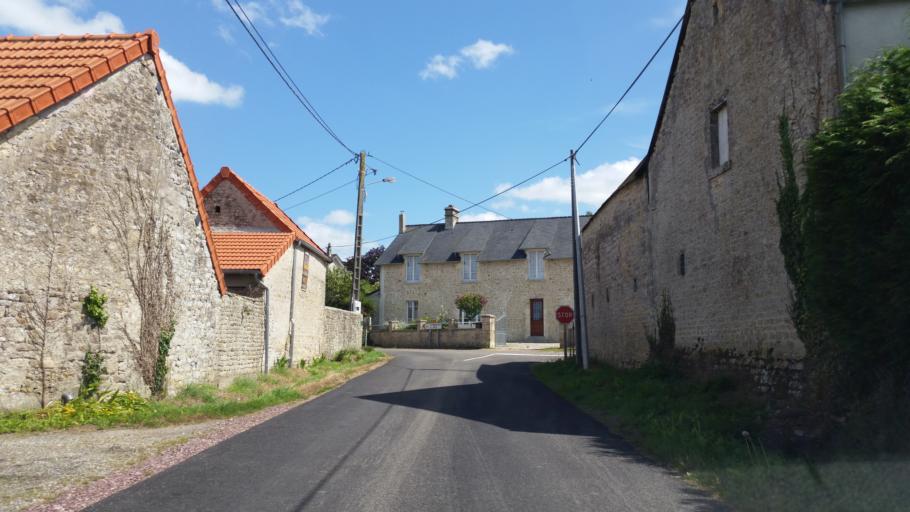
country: FR
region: Lower Normandy
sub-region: Departement de la Manche
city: Sainte-Mere-Eglise
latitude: 49.4581
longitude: -1.3189
